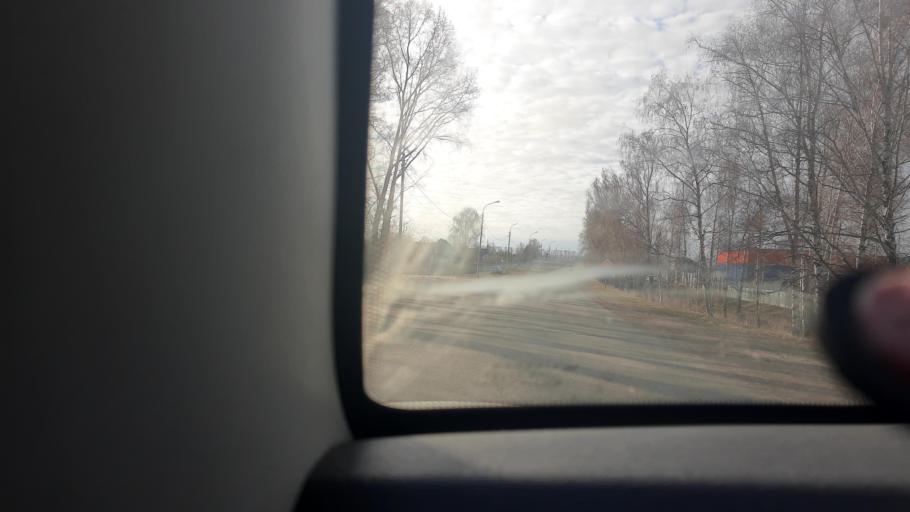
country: RU
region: Bashkortostan
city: Asanovo
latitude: 54.9599
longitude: 55.5503
